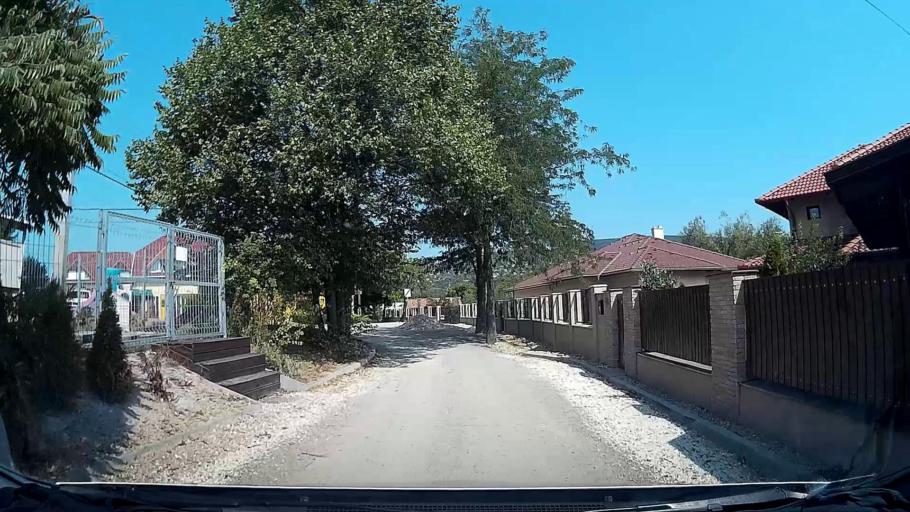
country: HU
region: Pest
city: Szentendre
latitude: 47.6865
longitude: 19.0514
